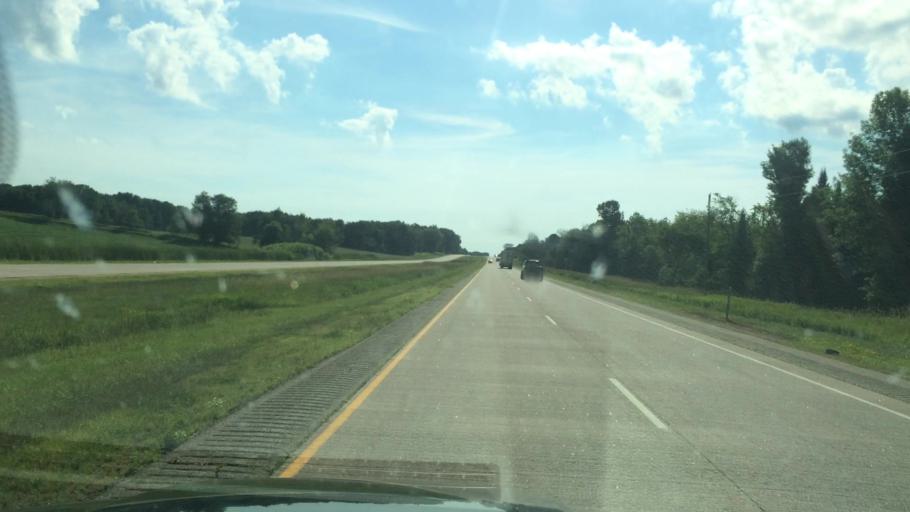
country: US
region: Wisconsin
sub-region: Waupaca County
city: Marion
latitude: 44.8040
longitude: -88.9900
